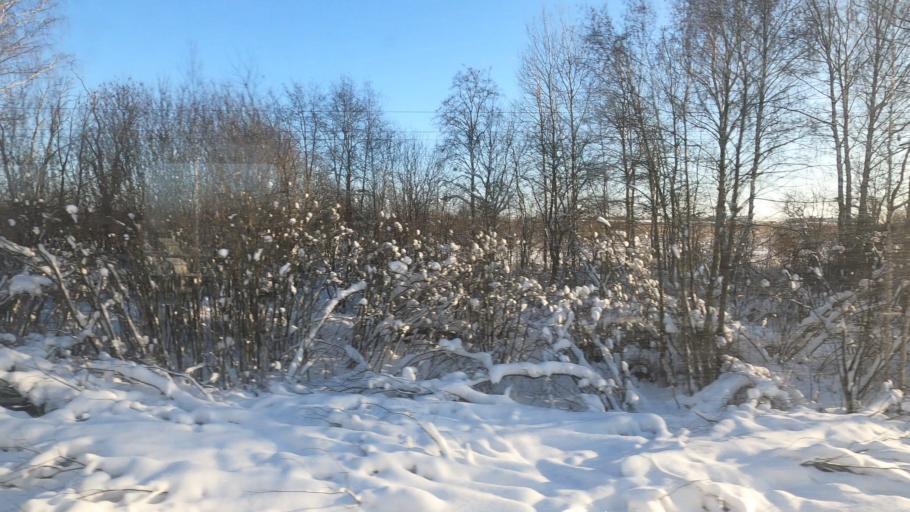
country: RU
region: Moskovskaya
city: Orud'yevo
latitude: 56.4301
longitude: 37.4999
